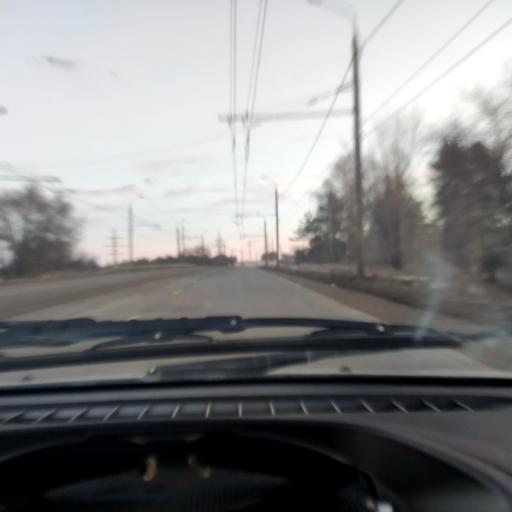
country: RU
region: Samara
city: Zhigulevsk
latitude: 53.5059
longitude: 49.5176
